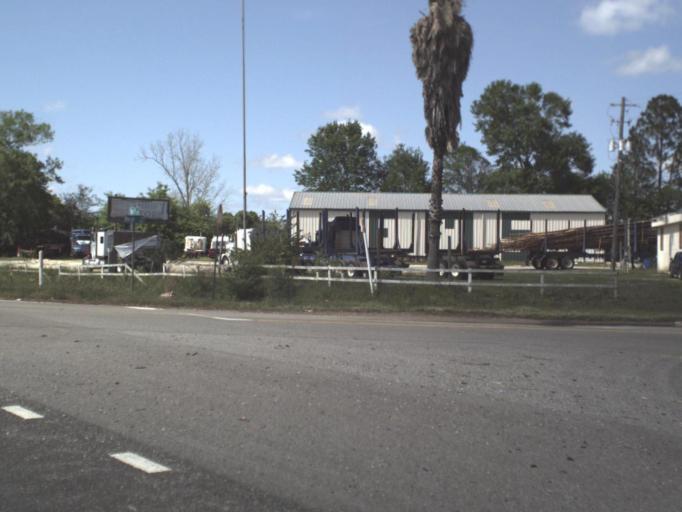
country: US
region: Florida
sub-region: Escambia County
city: Cantonment
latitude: 30.6289
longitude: -87.3317
